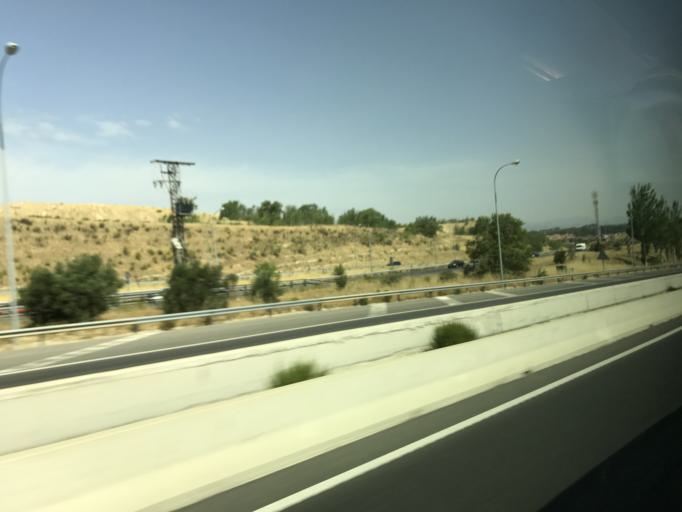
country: ES
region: Madrid
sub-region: Provincia de Madrid
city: San Blas
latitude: 40.4361
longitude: -3.5937
